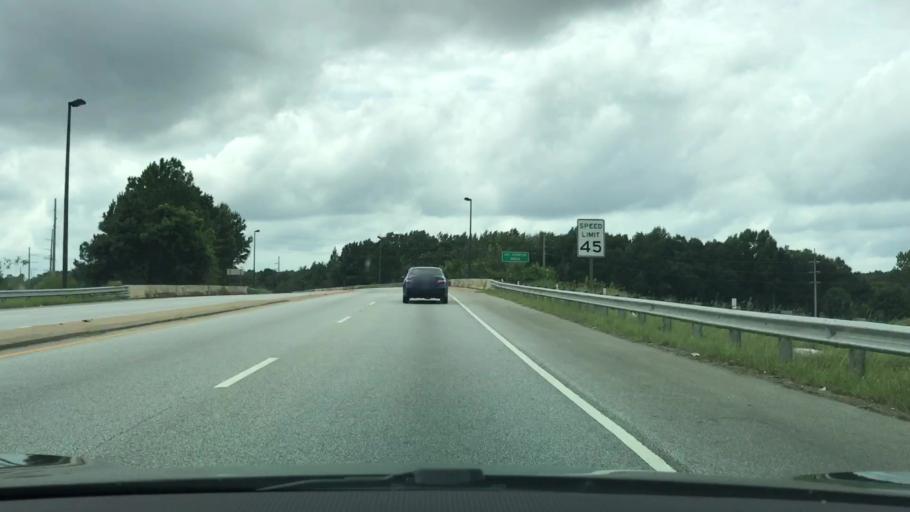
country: US
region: Alabama
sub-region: Lee County
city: Opelika
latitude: 32.6345
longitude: -85.4095
